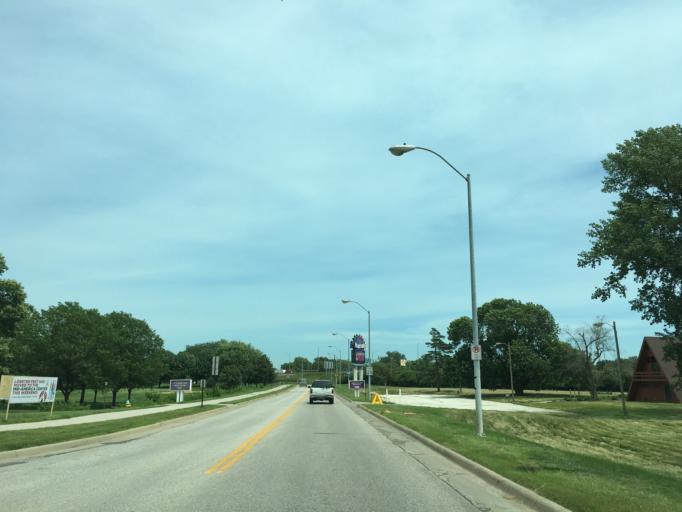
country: US
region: Nebraska
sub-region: Douglas County
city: Omaha
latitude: 41.2518
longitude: -95.9098
